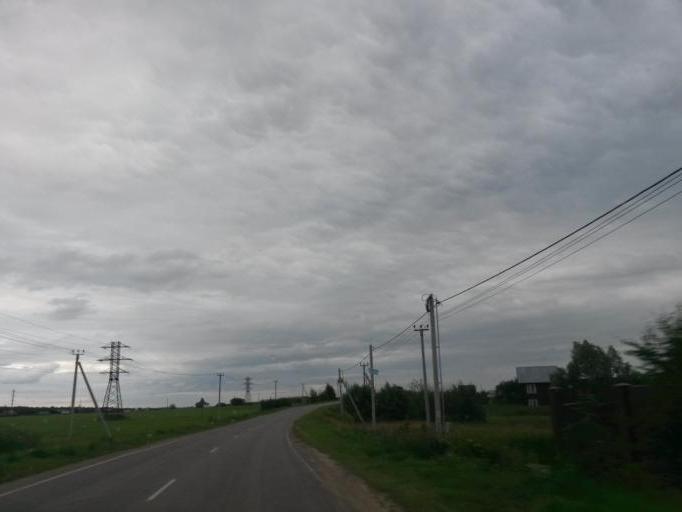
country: RU
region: Moskovskaya
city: Barybino
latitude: 55.2478
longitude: 37.7944
